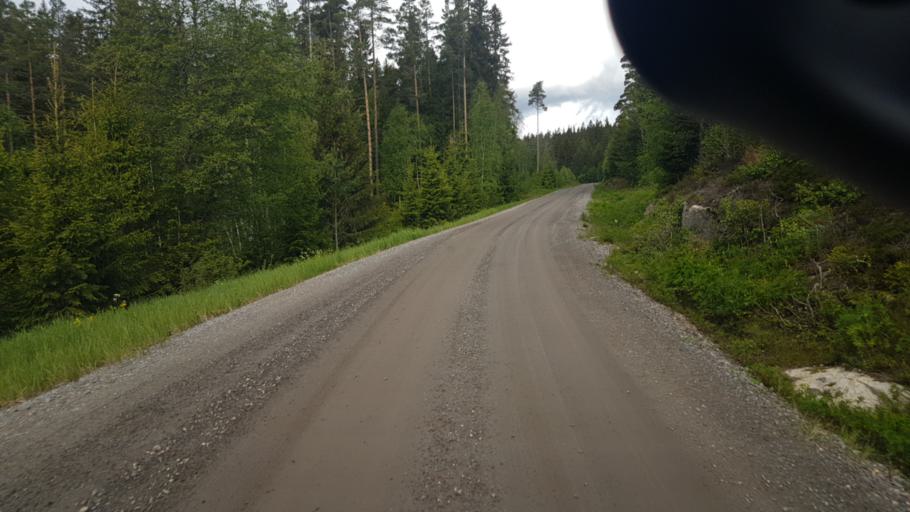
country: NO
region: Ostfold
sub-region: Romskog
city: Romskog
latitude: 59.7058
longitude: 12.0479
